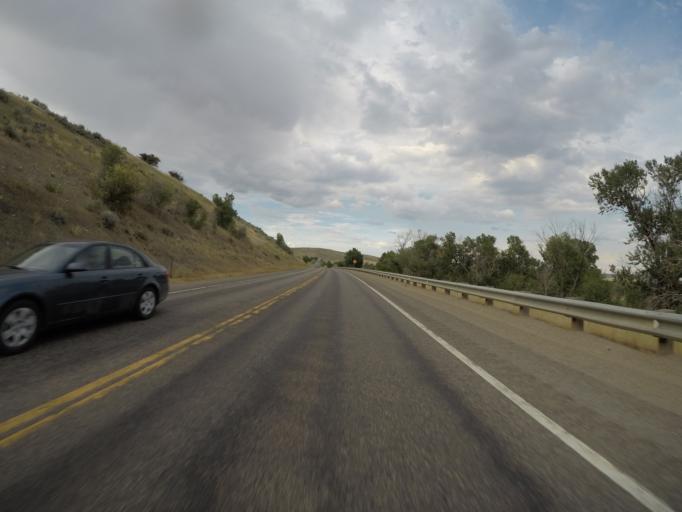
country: US
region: Colorado
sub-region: Moffat County
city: Craig
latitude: 40.5267
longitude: -107.4607
